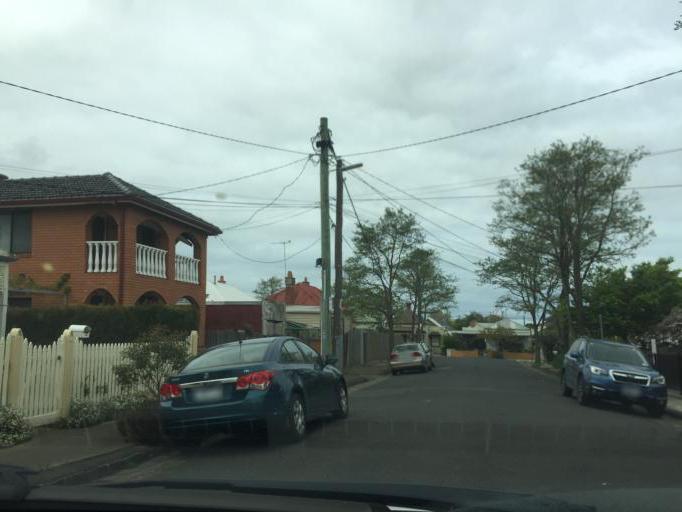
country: AU
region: Victoria
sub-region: Maribyrnong
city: Seddon
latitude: -37.8136
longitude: 144.8869
